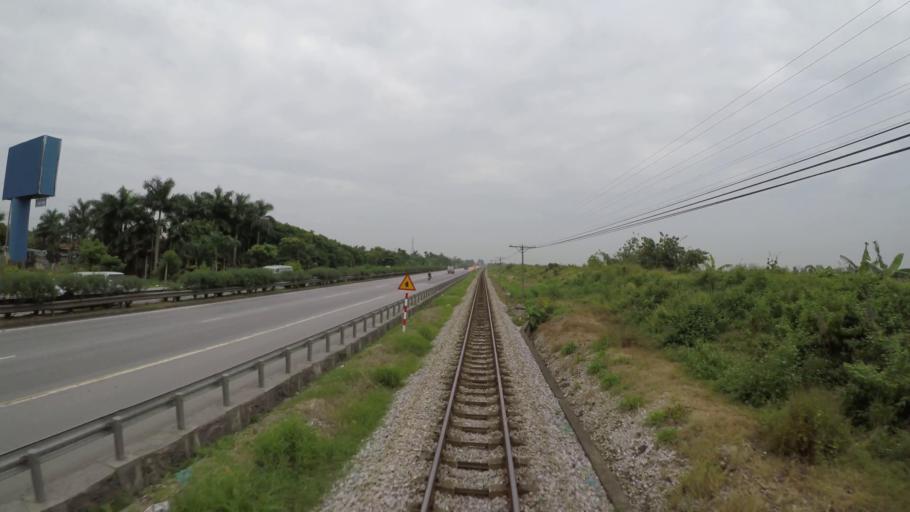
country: VN
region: Hai Duong
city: Nam Sach
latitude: 20.9763
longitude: 106.4017
